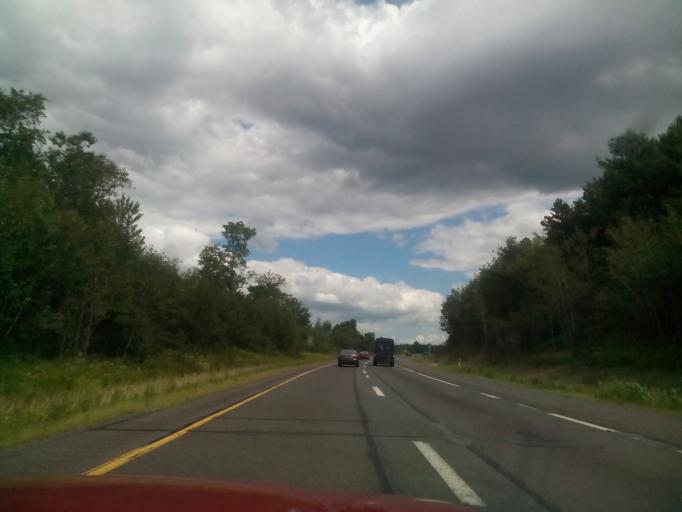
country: US
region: Pennsylvania
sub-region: Monroe County
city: Pocono Pines
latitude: 41.0780
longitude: -75.5120
